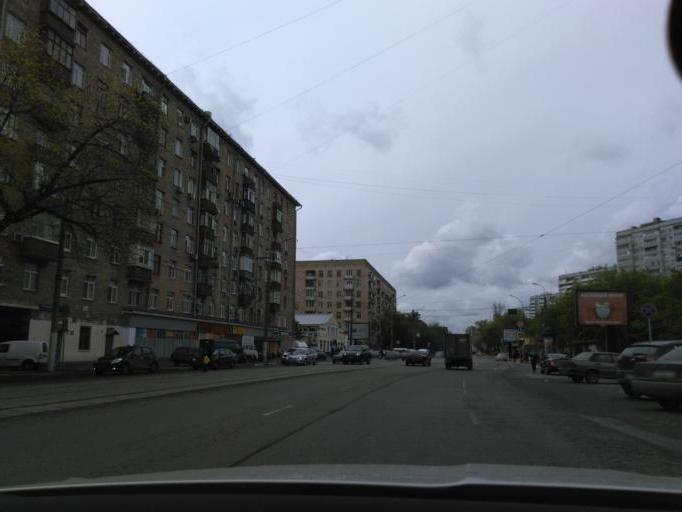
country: RU
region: Moscow
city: Taganskiy
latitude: 55.7457
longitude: 37.6791
